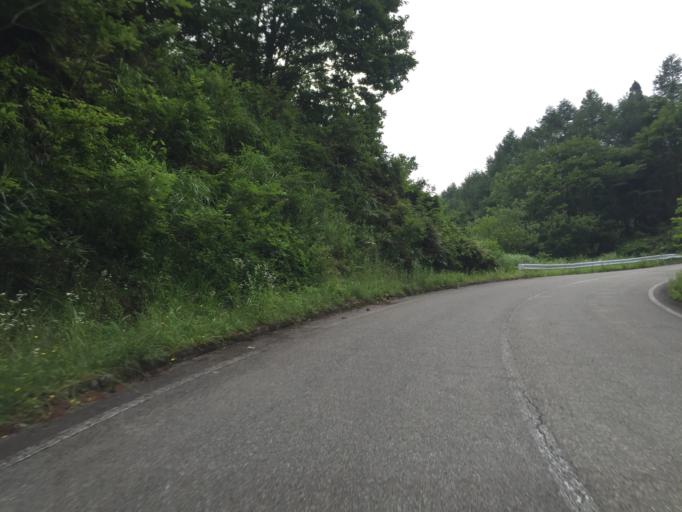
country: JP
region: Fukushima
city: Inawashiro
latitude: 37.6724
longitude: 140.1124
